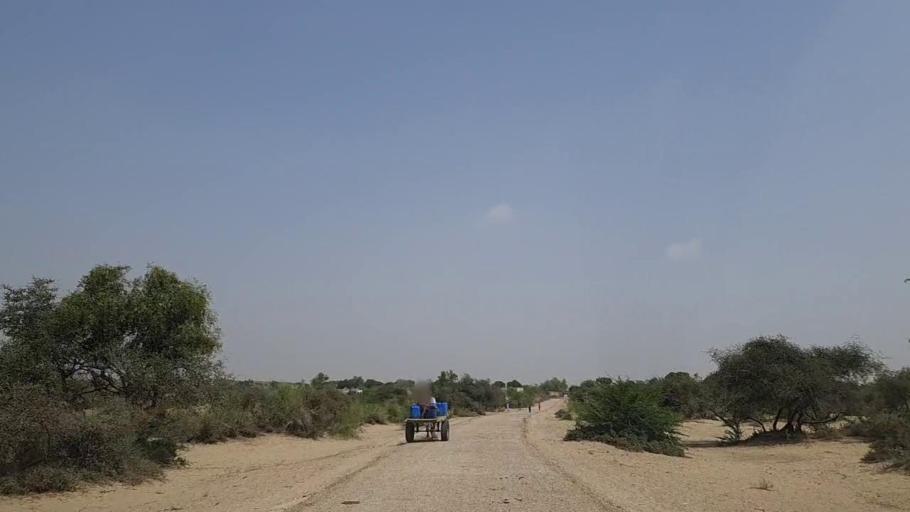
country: PK
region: Sindh
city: Mithi
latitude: 24.7592
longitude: 69.9283
